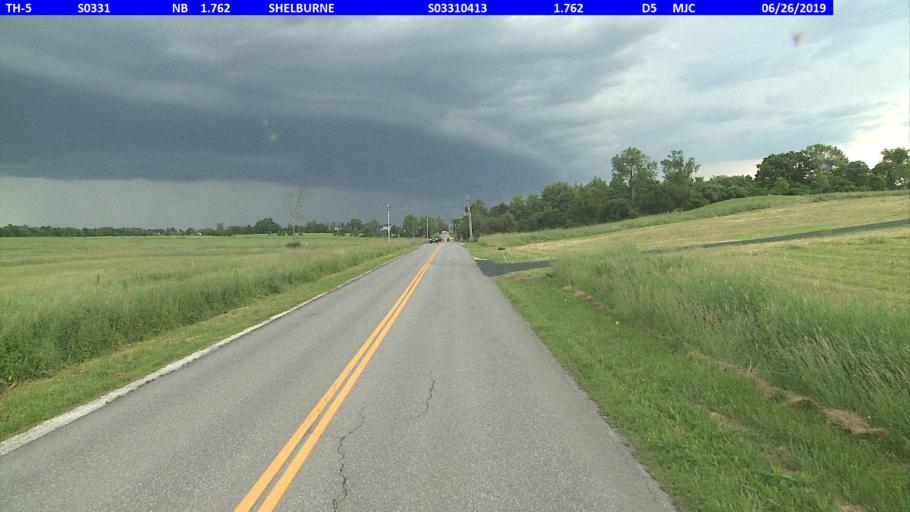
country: US
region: Vermont
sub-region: Chittenden County
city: South Burlington
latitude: 44.3960
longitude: -73.1763
